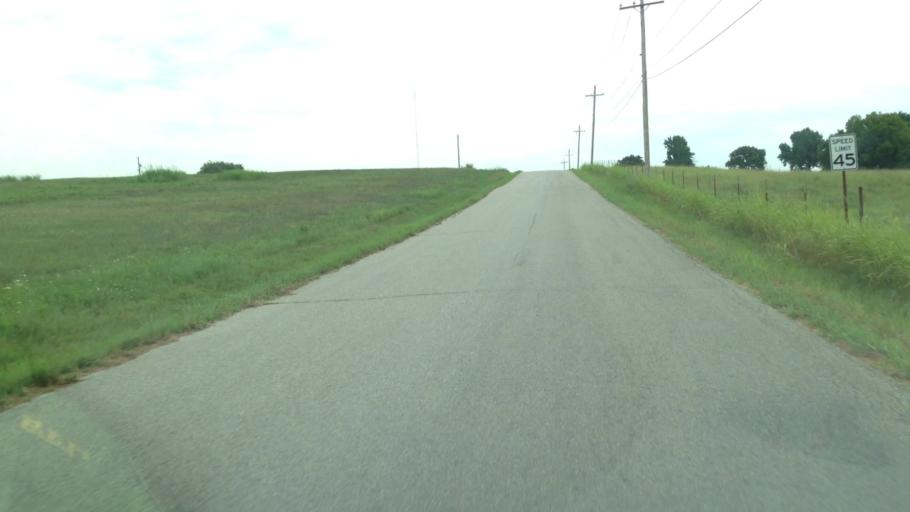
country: US
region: Oklahoma
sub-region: Craig County
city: Vinita
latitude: 36.6416
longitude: -95.1256
